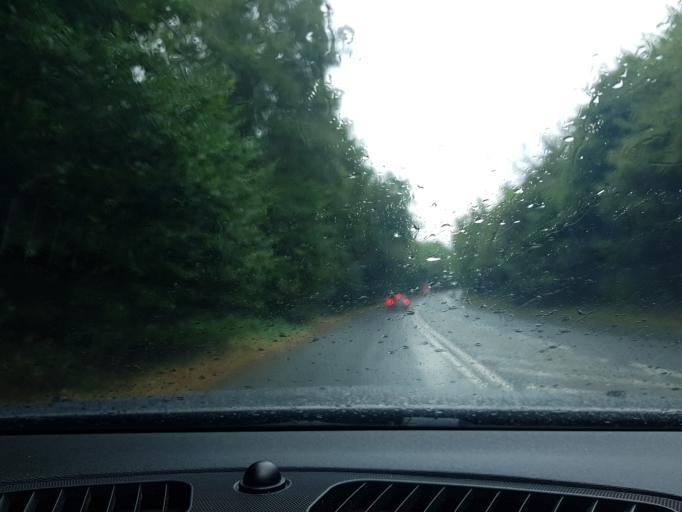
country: GB
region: England
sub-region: Surrey
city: Farnham
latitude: 51.2380
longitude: -0.8370
